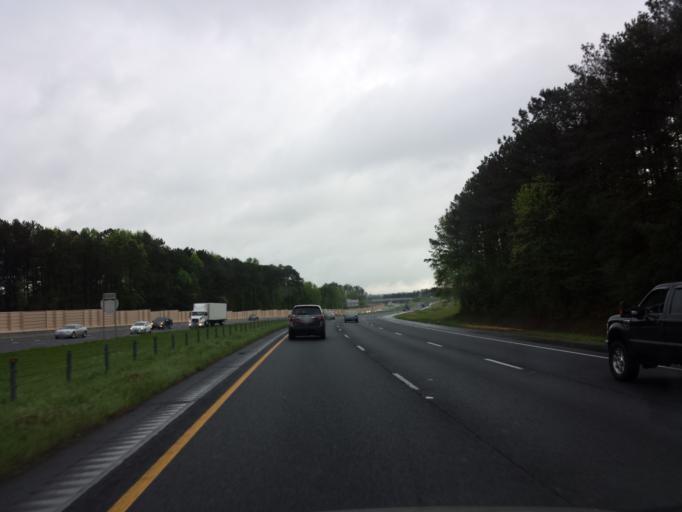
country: US
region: Georgia
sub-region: Cherokee County
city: Woodstock
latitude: 34.1155
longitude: -84.5330
